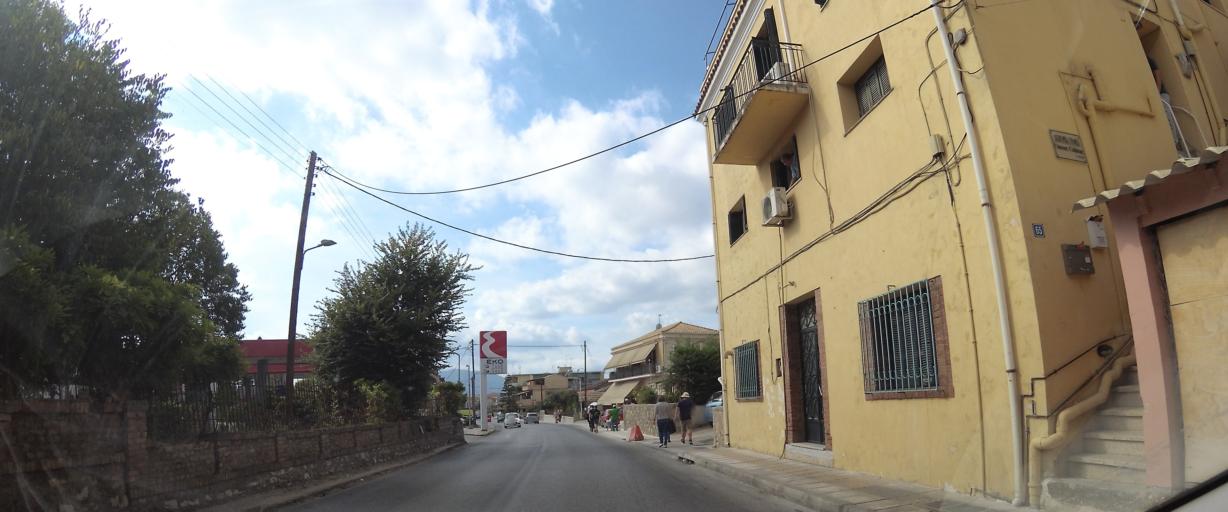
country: GR
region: Ionian Islands
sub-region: Nomos Kerkyras
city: Kerkyra
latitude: 39.6182
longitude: 19.9149
